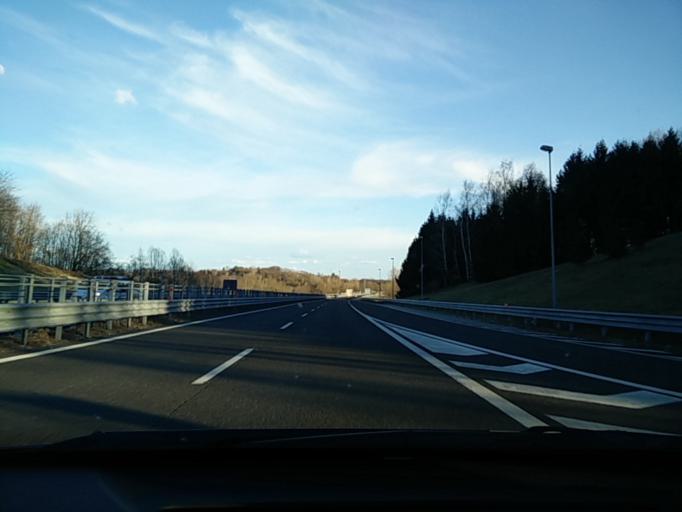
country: IT
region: Friuli Venezia Giulia
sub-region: Provincia di Udine
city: Collofedo di Monte Albano
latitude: 46.1674
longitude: 13.1549
